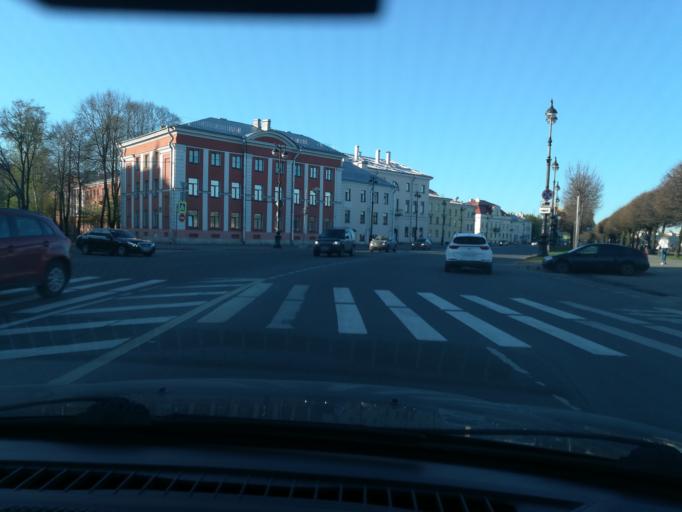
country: RU
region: St.-Petersburg
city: Vasyl'evsky Ostrov
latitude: 59.9295
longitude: 30.2703
